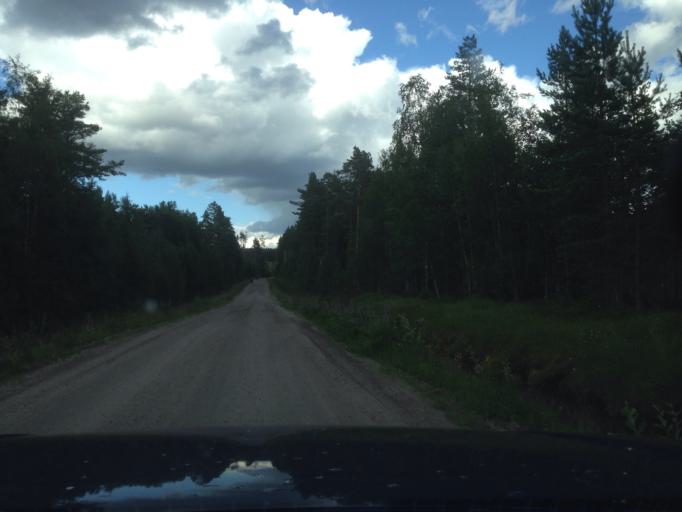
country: SE
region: Dalarna
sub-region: Vansbro Kommun
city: Jarna
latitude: 60.3267
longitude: 14.5480
